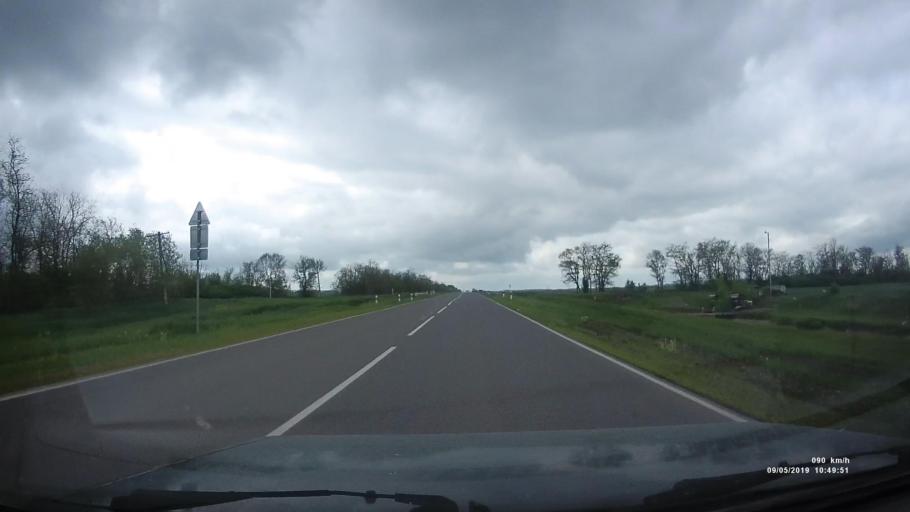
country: RU
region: Rostov
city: Peshkovo
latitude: 46.9368
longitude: 39.3554
